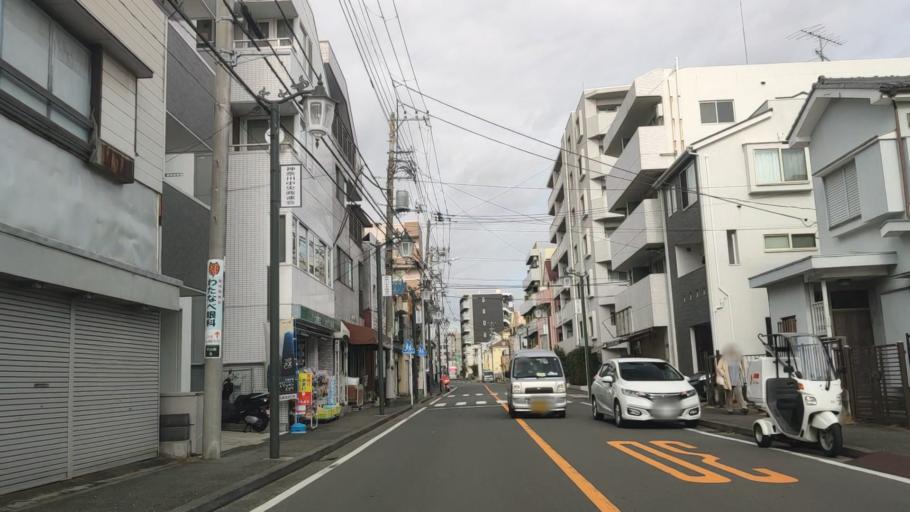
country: JP
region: Kanagawa
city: Yokohama
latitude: 35.4794
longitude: 139.6281
